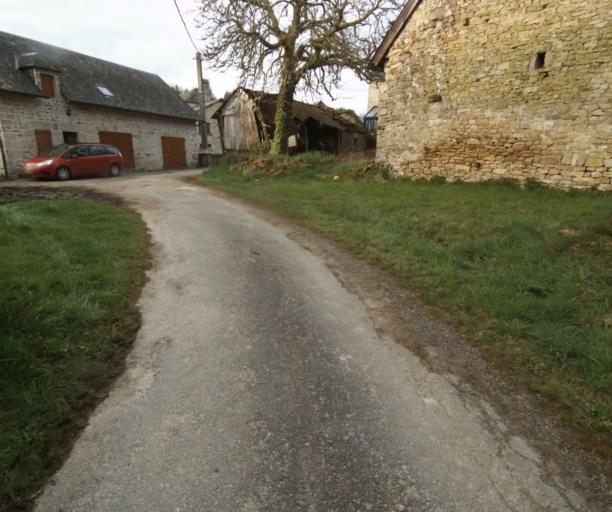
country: FR
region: Limousin
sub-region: Departement de la Correze
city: Correze
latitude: 45.3960
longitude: 1.8694
